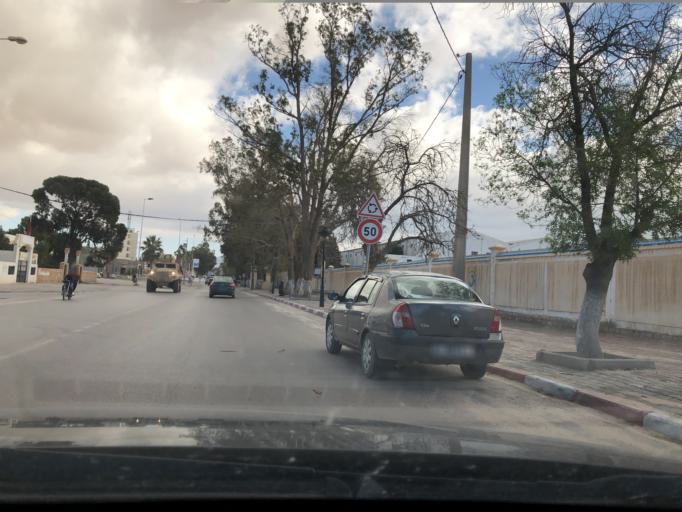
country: TN
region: Al Qasrayn
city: Kasserine
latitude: 35.1681
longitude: 8.8192
